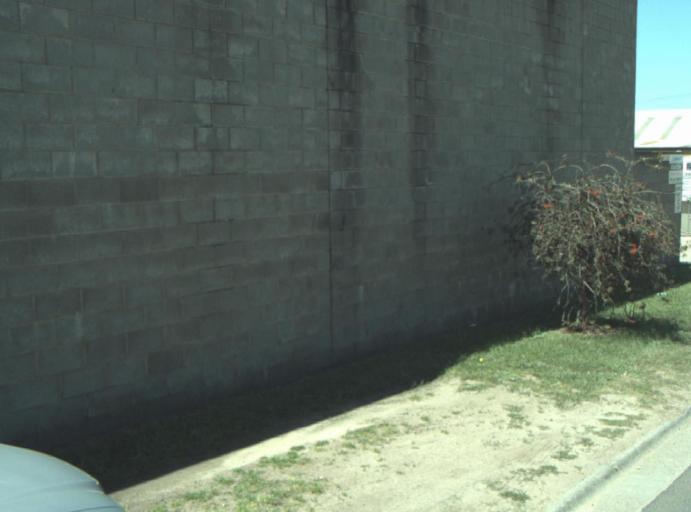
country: AU
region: Victoria
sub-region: Greater Geelong
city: Bell Park
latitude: -38.1012
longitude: 144.3457
